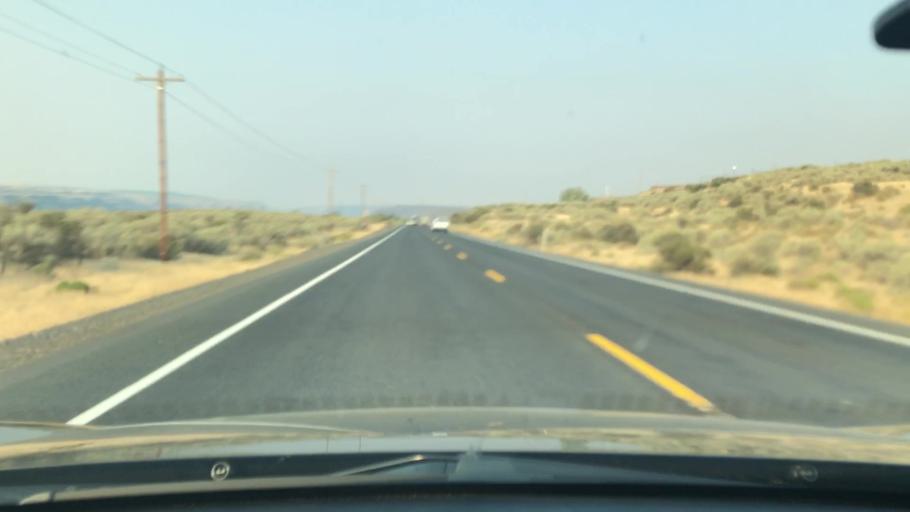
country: US
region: Oregon
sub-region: Umatilla County
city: Stanfield
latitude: 45.9182
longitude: -119.1282
